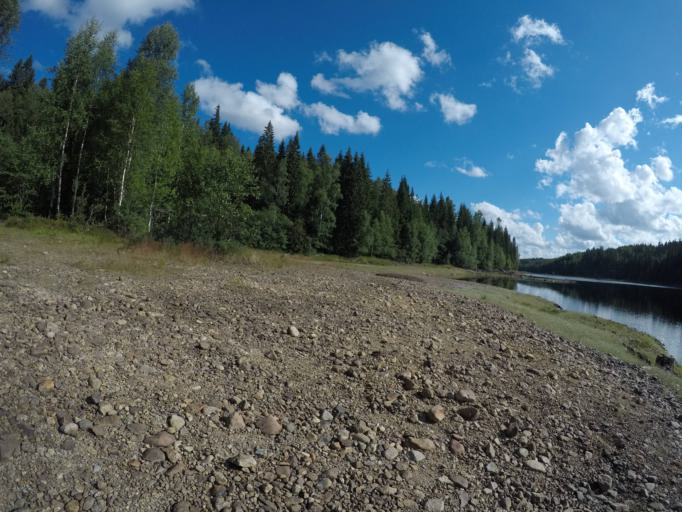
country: SE
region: OErebro
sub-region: Hallefors Kommun
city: Haellefors
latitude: 59.9991
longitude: 14.6050
